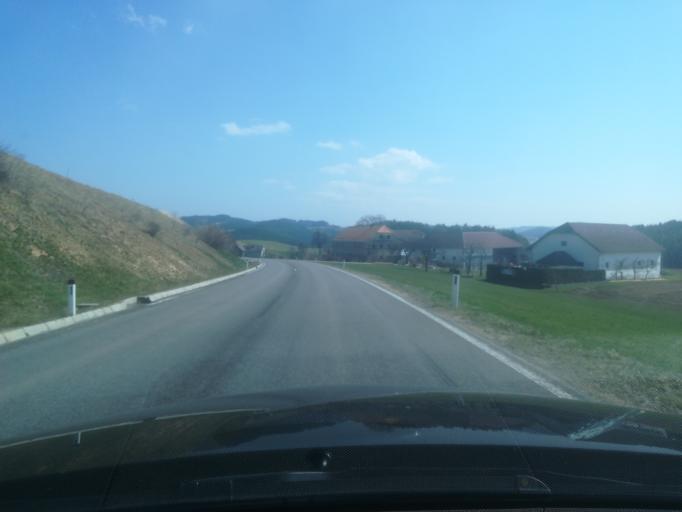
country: AT
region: Upper Austria
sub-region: Politischer Bezirk Perg
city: Bad Kreuzen
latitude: 48.4160
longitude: 14.7436
